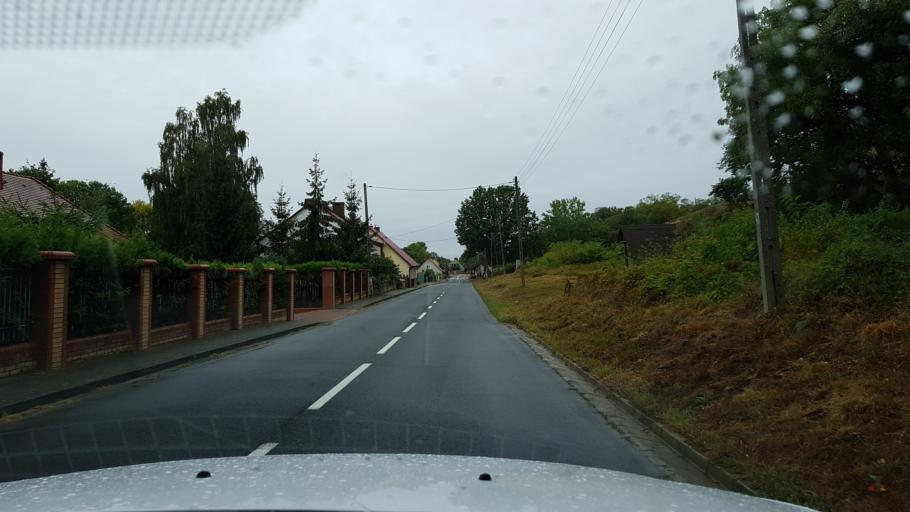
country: PL
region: West Pomeranian Voivodeship
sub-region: Powiat gryfinski
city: Cedynia
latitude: 52.8324
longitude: 14.1487
